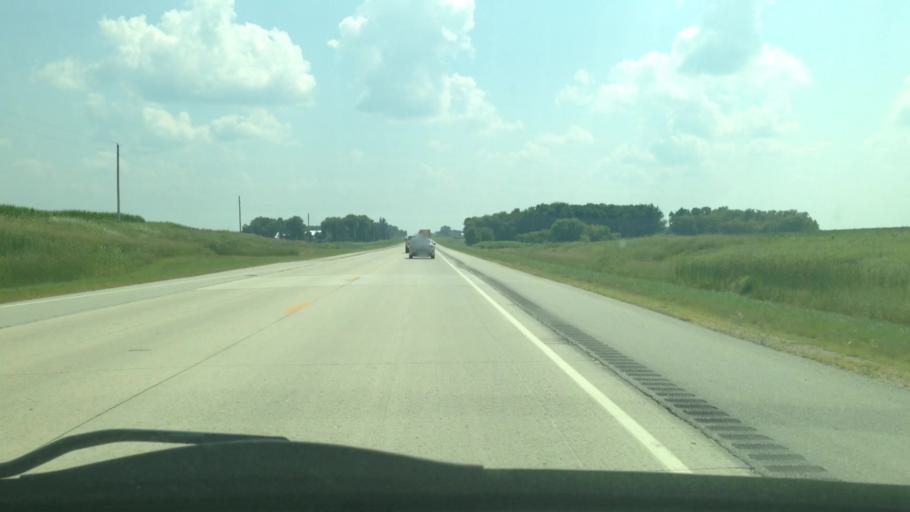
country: US
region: Minnesota
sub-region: Fillmore County
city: Spring Valley
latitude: 43.5287
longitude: -92.3694
